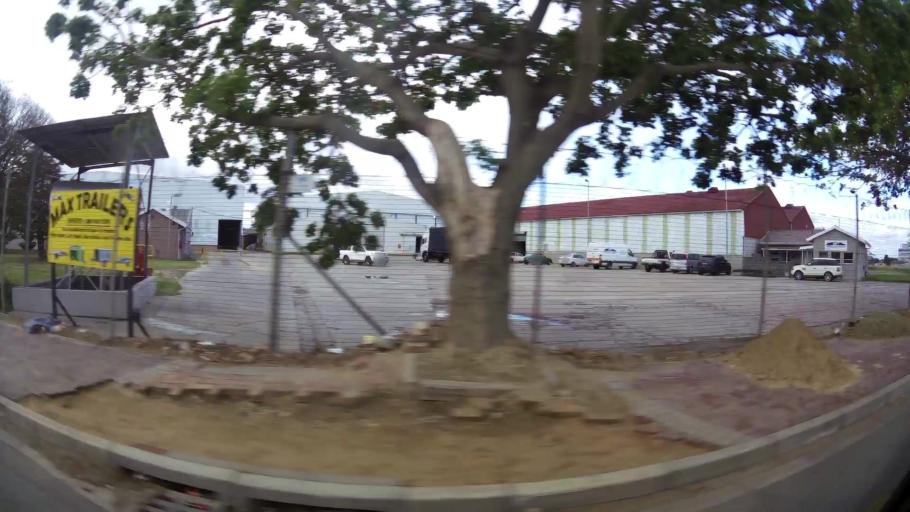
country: ZA
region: Western Cape
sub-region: Eden District Municipality
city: George
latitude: -33.9768
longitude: 22.4716
